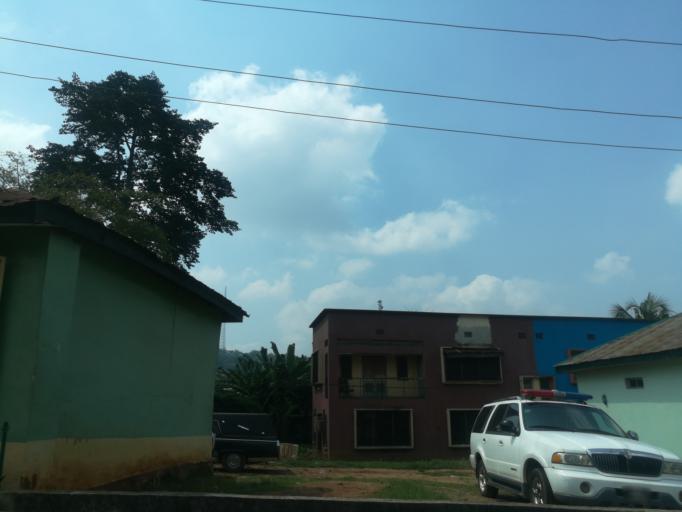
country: NG
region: Oyo
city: Ibadan
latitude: 7.4010
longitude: 3.8983
